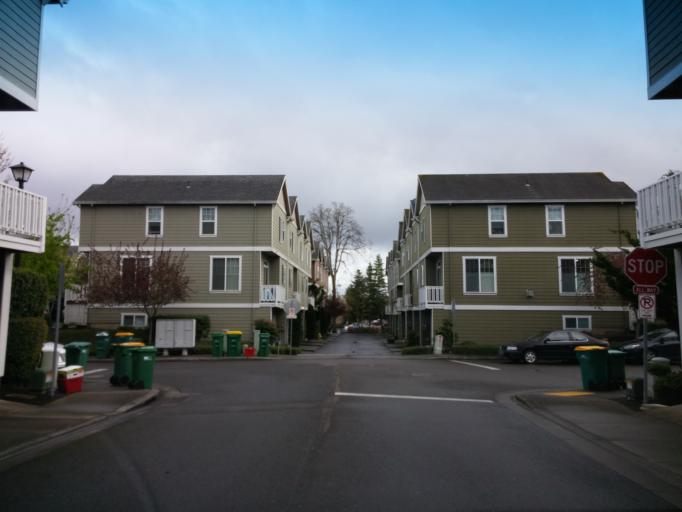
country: US
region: Oregon
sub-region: Washington County
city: Oak Hills
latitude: 45.5116
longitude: -122.8425
